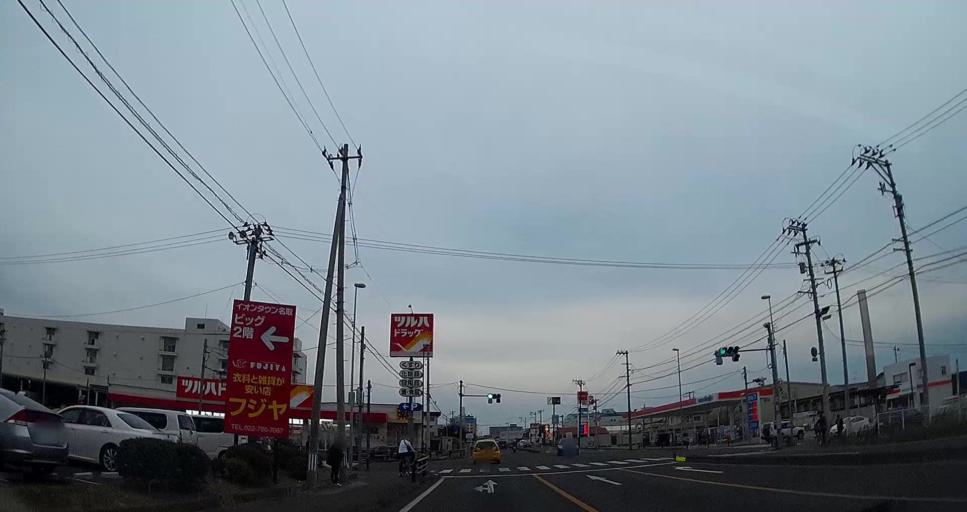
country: JP
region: Miyagi
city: Iwanuma
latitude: 38.1578
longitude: 140.8880
